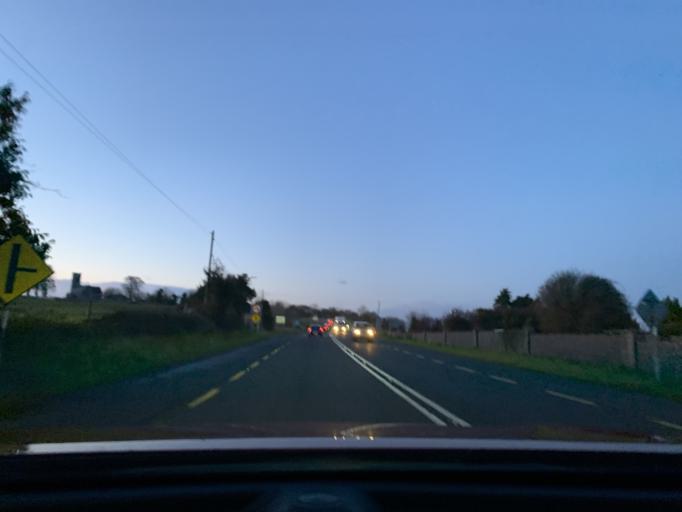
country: IE
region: Connaught
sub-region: Roscommon
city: Boyle
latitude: 53.9666
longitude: -8.1990
